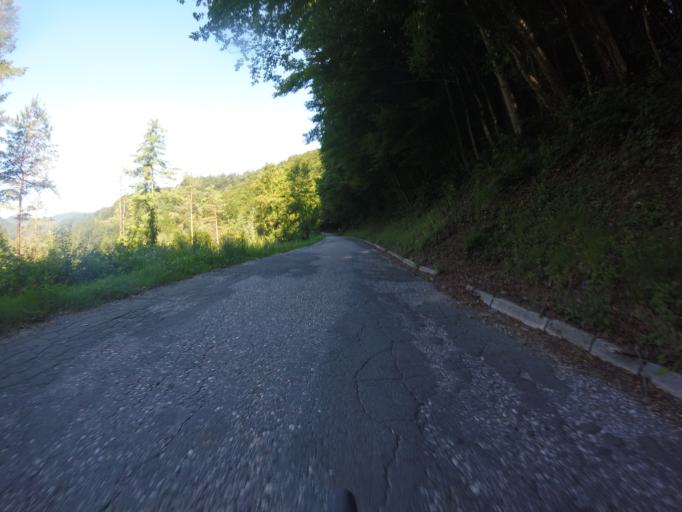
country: SI
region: Brezice
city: Brezice
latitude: 45.8371
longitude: 15.6070
